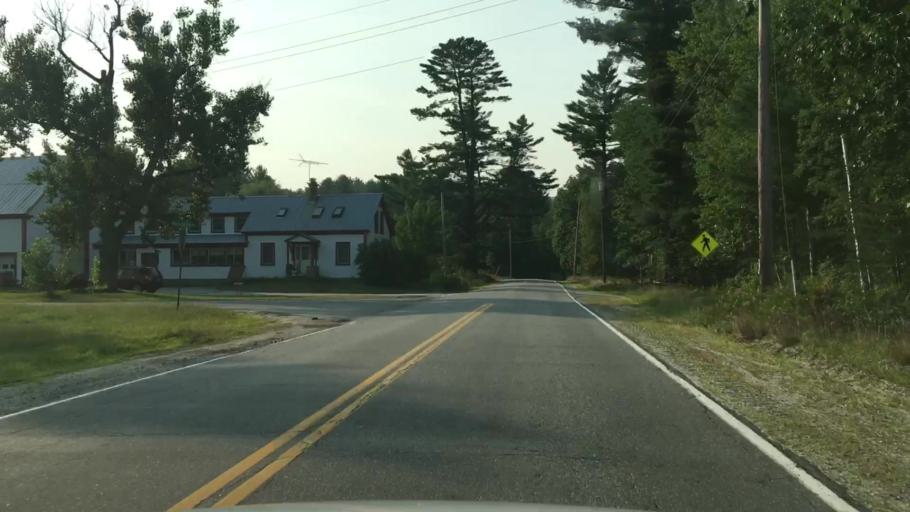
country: US
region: Maine
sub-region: Oxford County
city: Bethel
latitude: 44.3477
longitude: -70.7881
